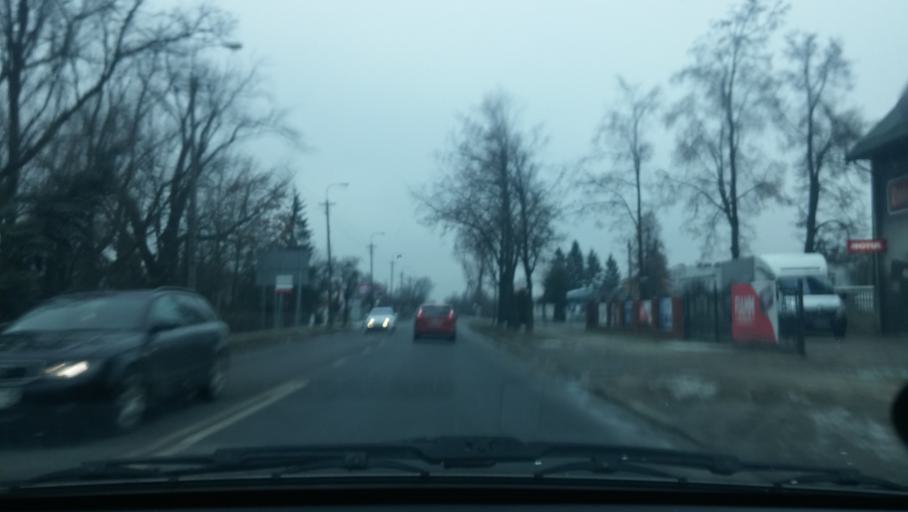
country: PL
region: Masovian Voivodeship
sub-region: Siedlce
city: Siedlce
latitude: 52.1854
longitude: 22.2679
